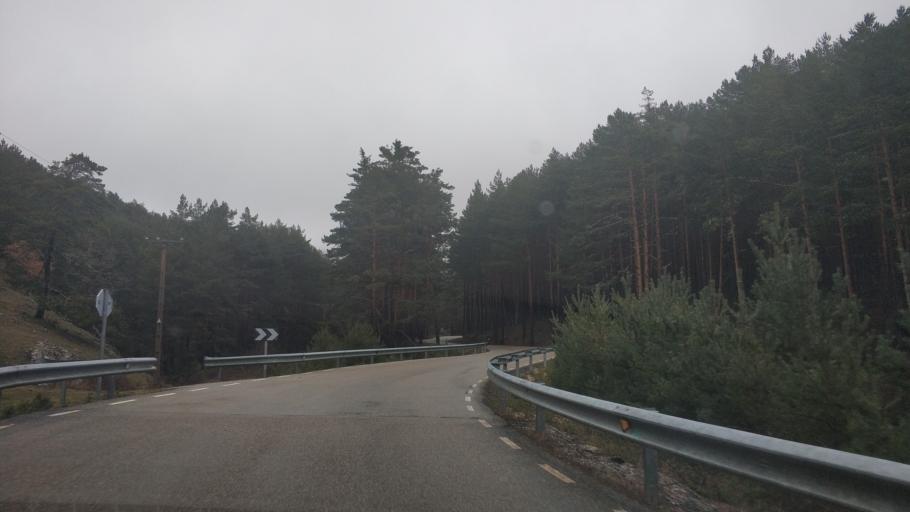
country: ES
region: Castille and Leon
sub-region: Provincia de Burgos
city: Neila
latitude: 42.0283
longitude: -3.0100
